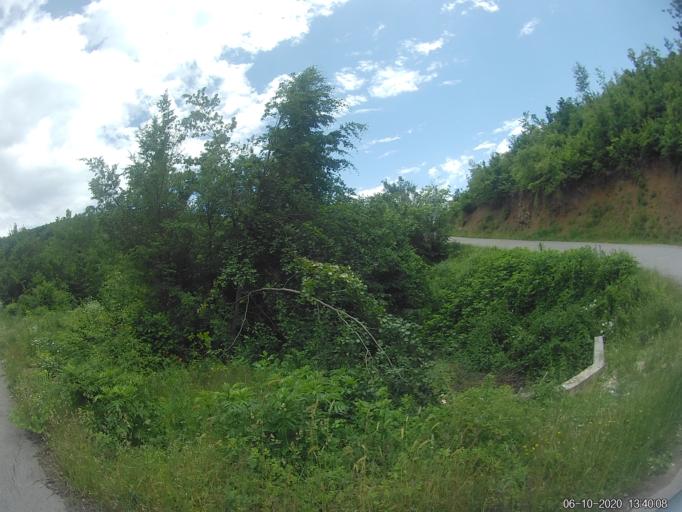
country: XK
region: Prizren
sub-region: Komuna e Therandes
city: Budakovo
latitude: 42.4160
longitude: 20.9149
